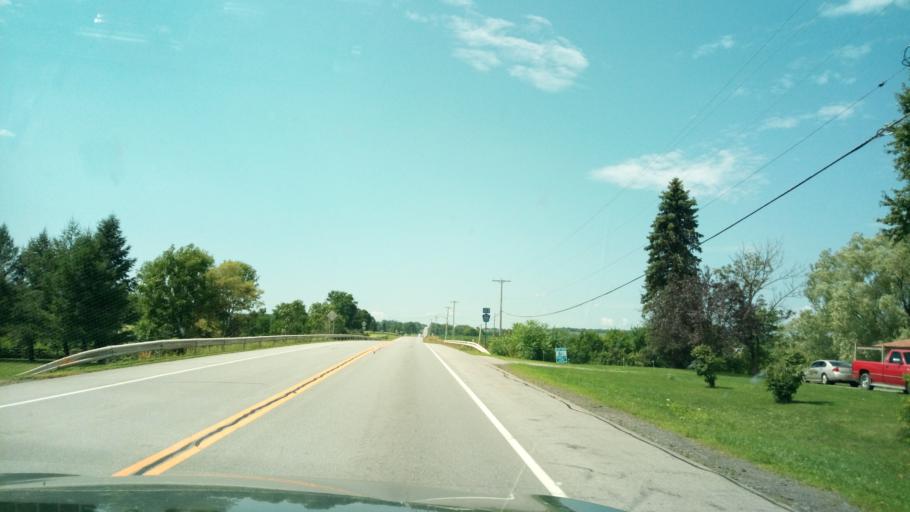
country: US
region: New York
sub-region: Livingston County
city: Geneseo
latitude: 42.8311
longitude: -77.9130
